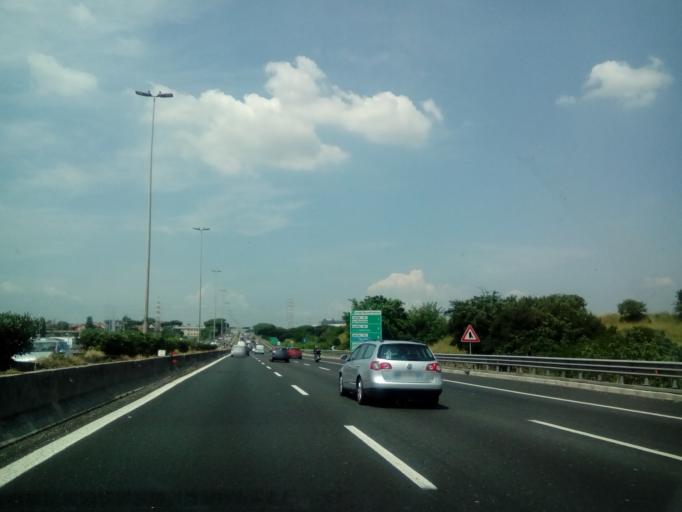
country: IT
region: Latium
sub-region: Citta metropolitana di Roma Capitale
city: Setteville
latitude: 41.8995
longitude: 12.6154
